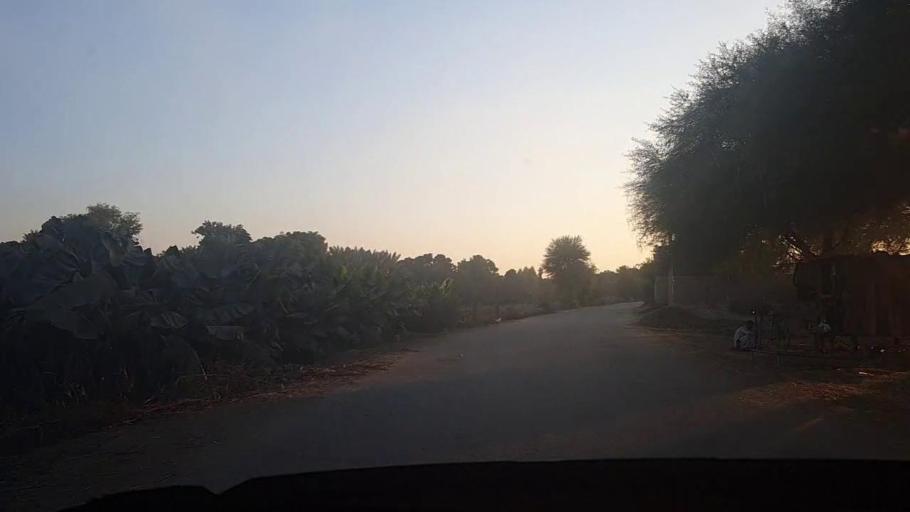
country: PK
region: Sindh
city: Sobhadero
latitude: 27.3388
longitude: 68.3789
